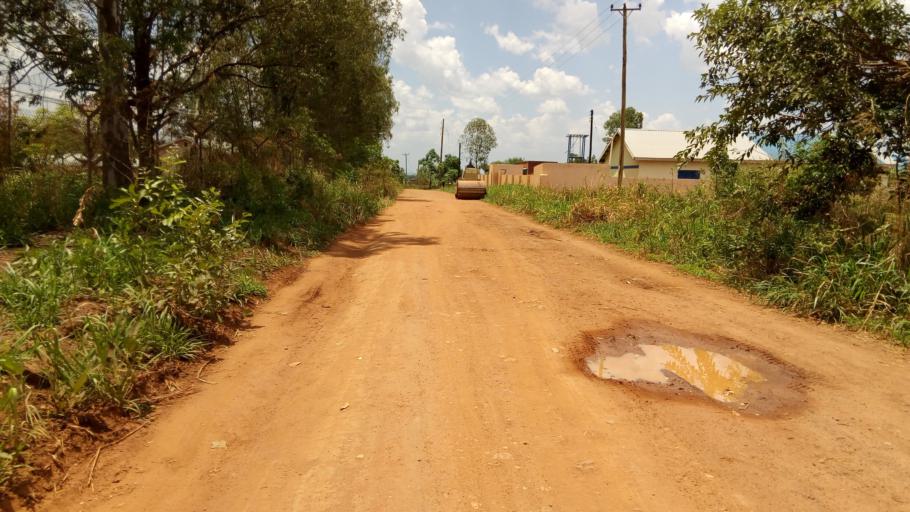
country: UG
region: Northern Region
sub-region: Gulu District
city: Gulu
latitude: 2.7910
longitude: 32.3490
